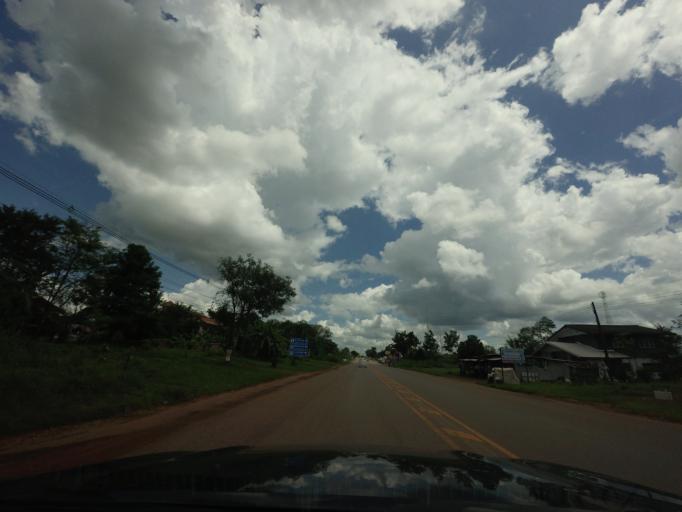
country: TH
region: Changwat Udon Thani
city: Ban Dung
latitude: 17.6775
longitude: 103.2465
